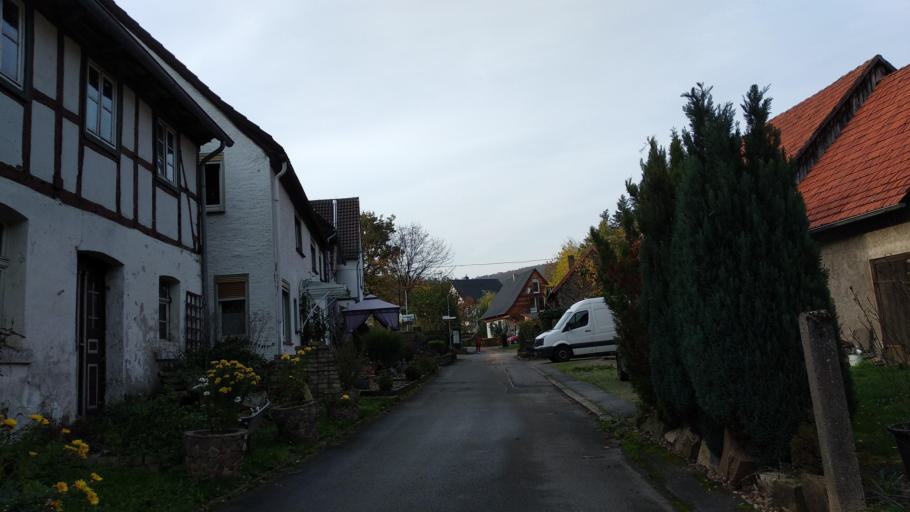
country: DE
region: North Rhine-Westphalia
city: Beverungen
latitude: 51.6933
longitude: 9.3864
